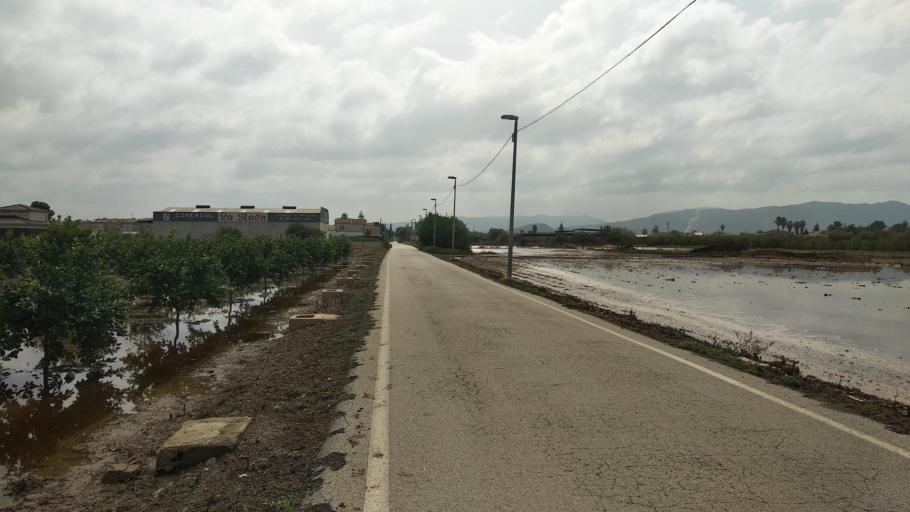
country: ES
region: Murcia
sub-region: Murcia
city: Santomera
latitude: 38.0432
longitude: -1.0358
